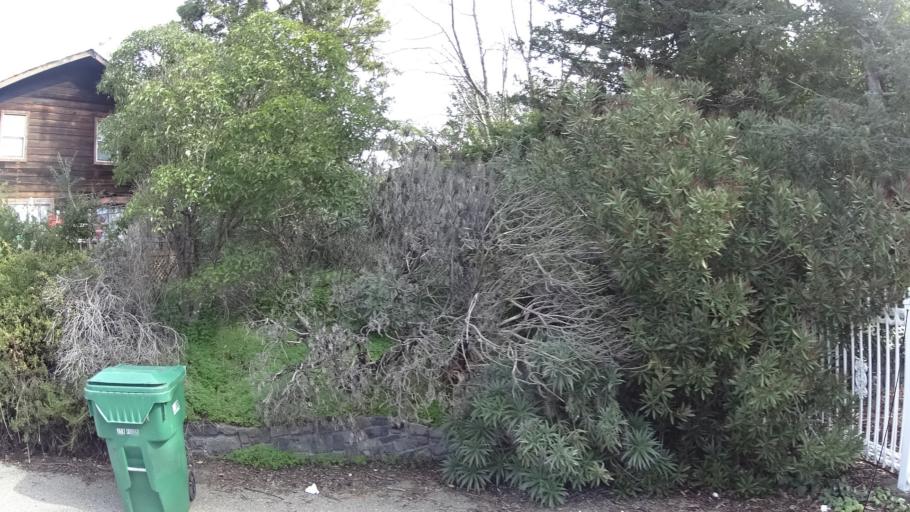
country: US
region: California
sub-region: Alameda County
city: Fairview
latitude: 37.6766
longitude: -122.0598
